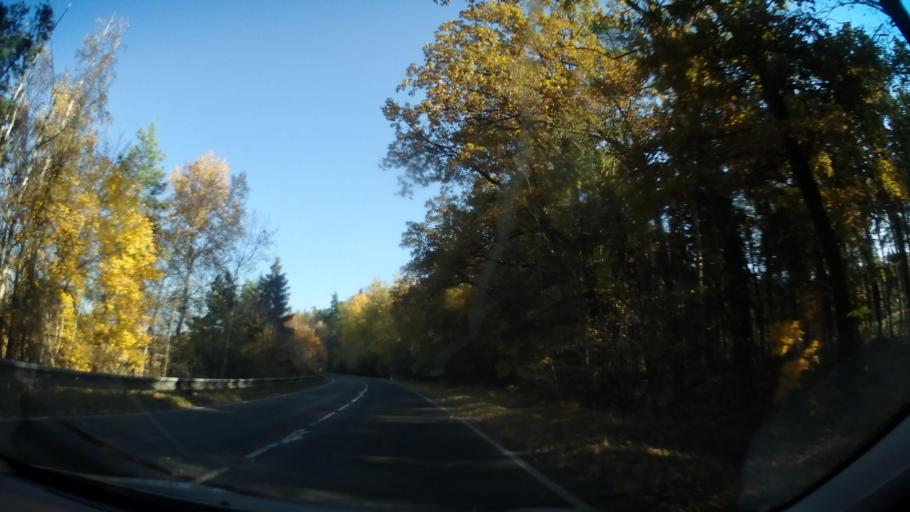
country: CZ
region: Kralovehradecky
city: Trebechovice pod Orebem
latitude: 50.2068
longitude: 16.0198
